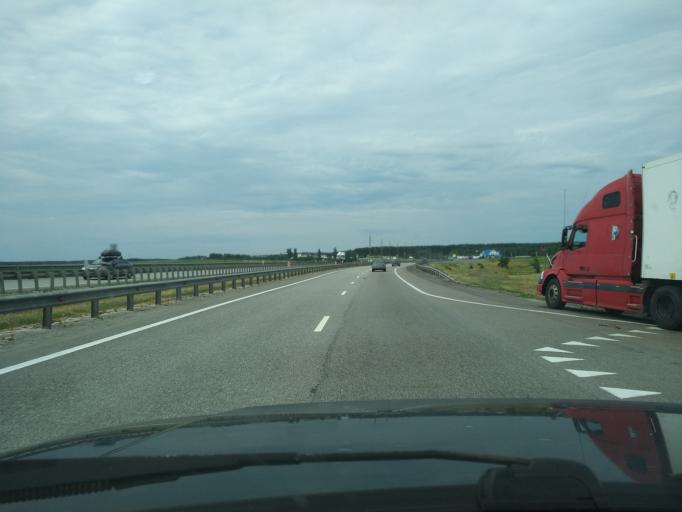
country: RU
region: Lipetsk
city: Khlevnoye
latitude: 52.0685
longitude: 39.1800
